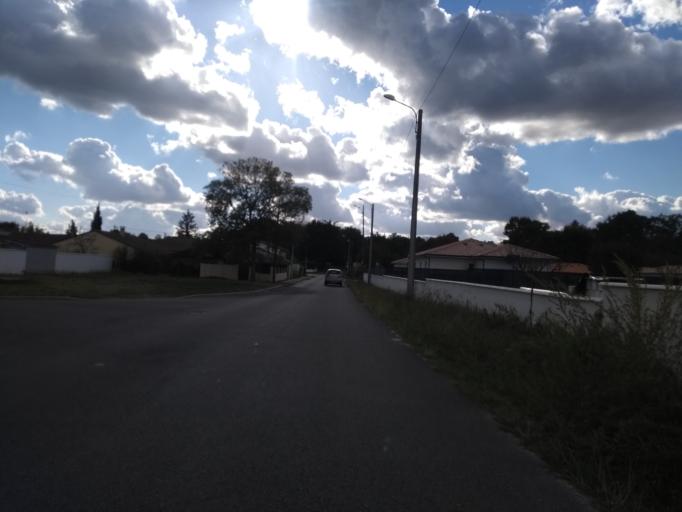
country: FR
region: Aquitaine
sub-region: Departement de la Gironde
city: Cestas
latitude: 44.7400
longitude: -0.6613
